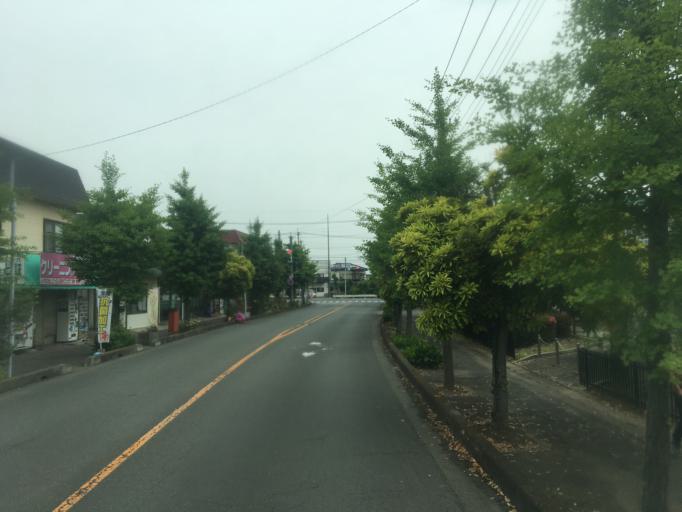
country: JP
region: Saitama
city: Sakado
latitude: 35.9879
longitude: 139.4451
